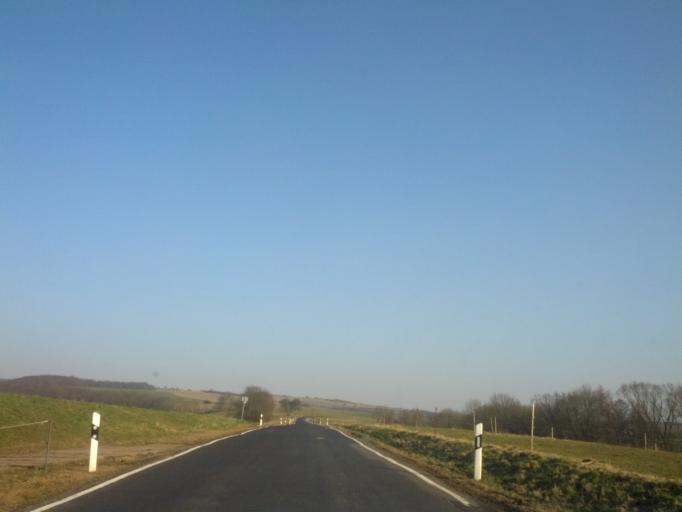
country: DE
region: Thuringia
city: Bischofroda
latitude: 51.0536
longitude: 10.3719
